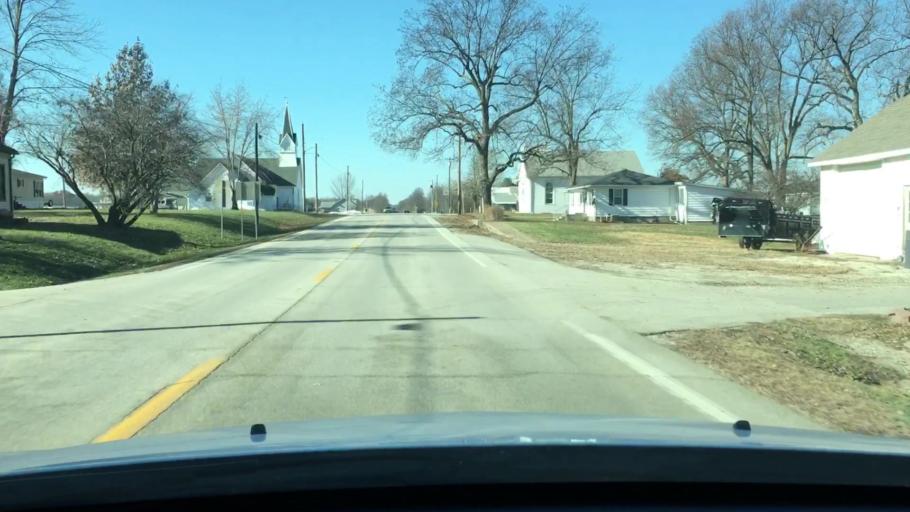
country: US
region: Illinois
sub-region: Pike County
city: Griggsville
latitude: 39.6202
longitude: -90.6778
